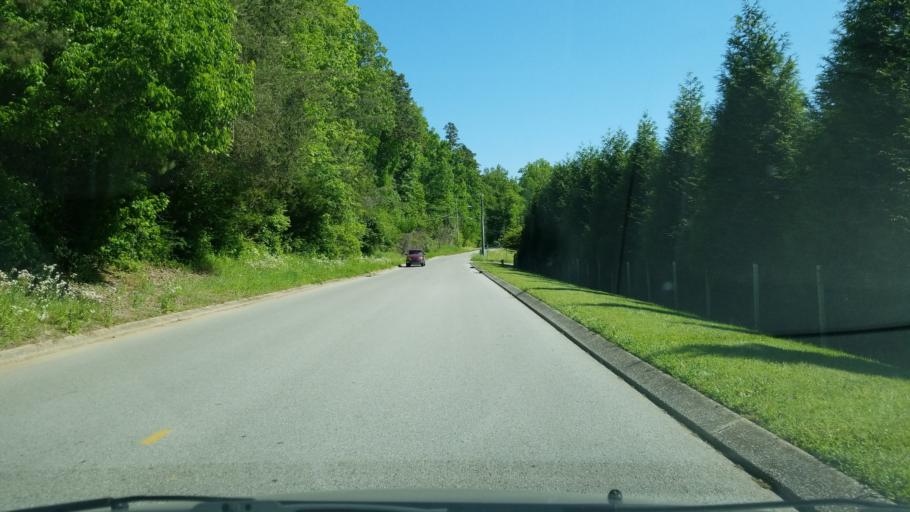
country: US
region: Tennessee
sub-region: Hamilton County
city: Walden
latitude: 35.1463
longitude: -85.2991
